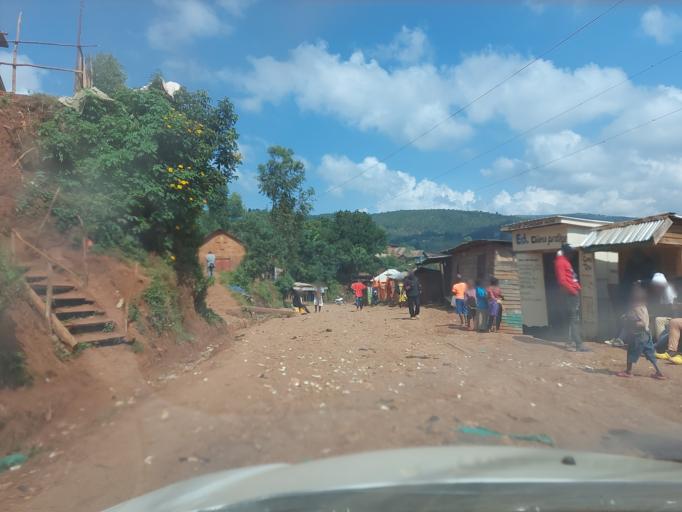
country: CD
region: South Kivu
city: Bukavu
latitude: -2.5124
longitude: 28.8361
